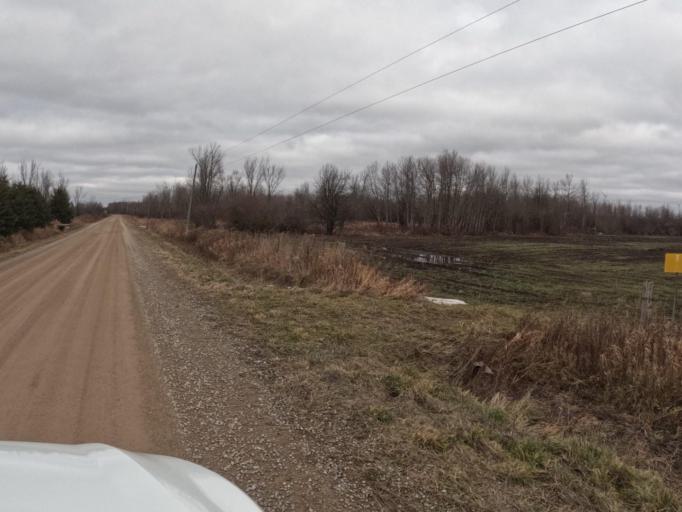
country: CA
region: Ontario
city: Shelburne
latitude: 43.8934
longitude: -80.3838
